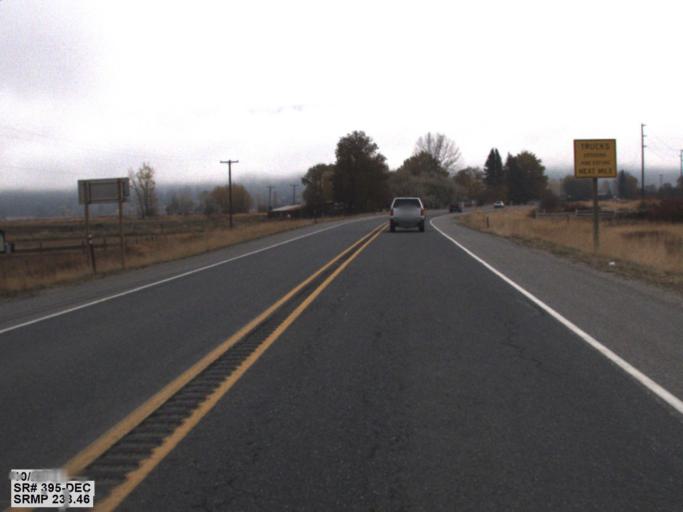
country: US
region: Washington
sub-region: Stevens County
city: Colville
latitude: 48.5836
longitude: -117.9648
